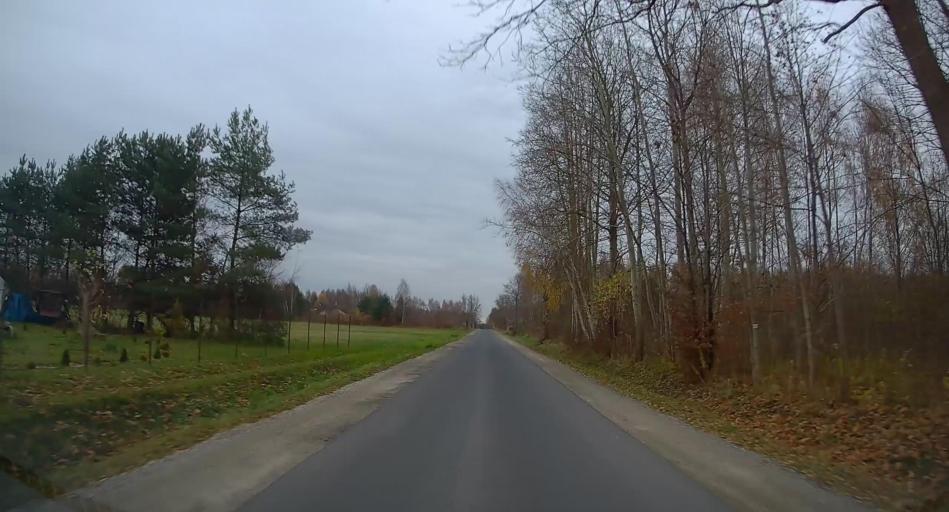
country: PL
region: Lodz Voivodeship
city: Zabia Wola
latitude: 51.9968
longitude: 20.6590
